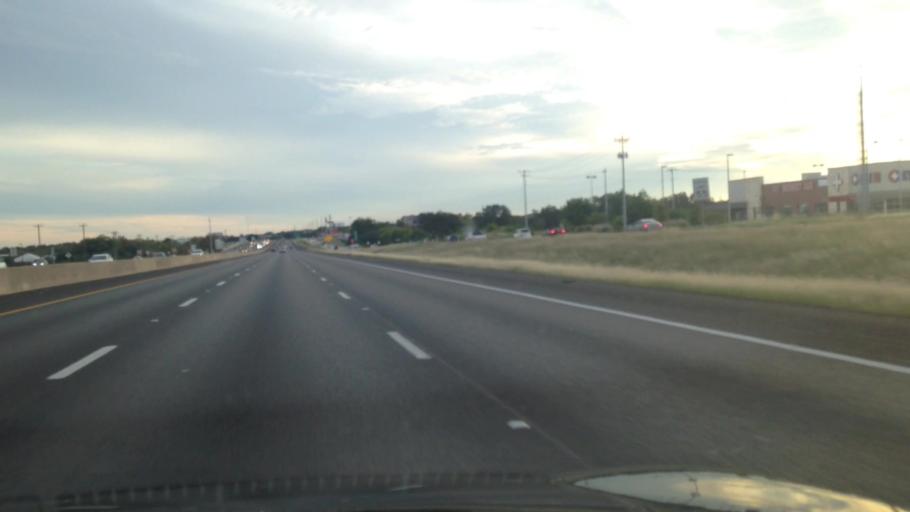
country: US
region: Texas
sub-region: Hays County
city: Kyle
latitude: 30.0078
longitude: -97.8643
